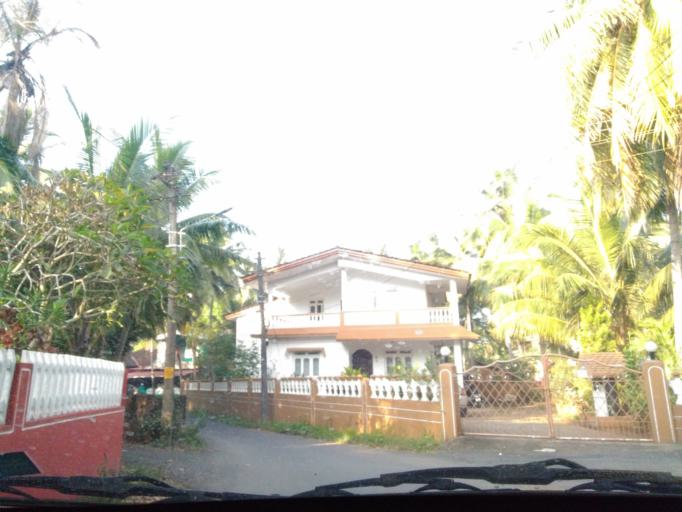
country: IN
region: Goa
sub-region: South Goa
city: Chinchinim
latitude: 15.2103
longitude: 73.9756
